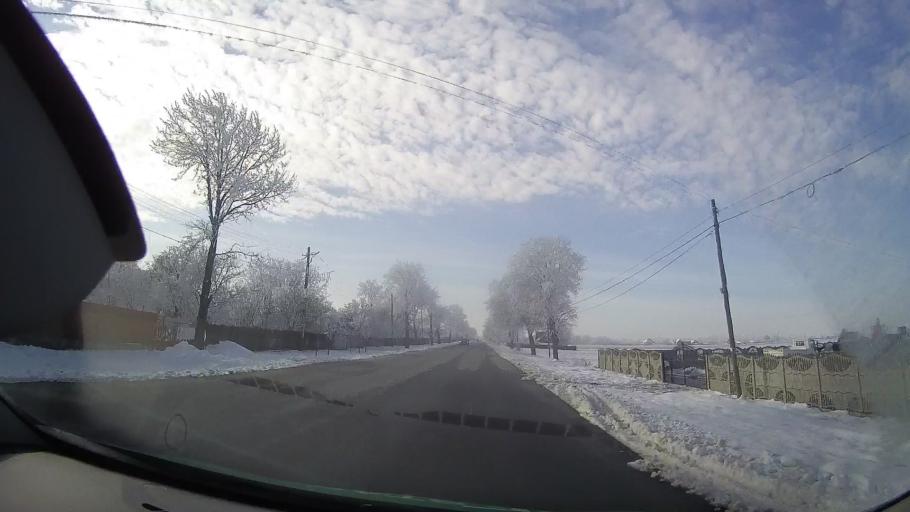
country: RO
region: Neamt
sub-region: Comuna Timisesti
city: Timisesti
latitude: 47.2312
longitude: 26.5152
